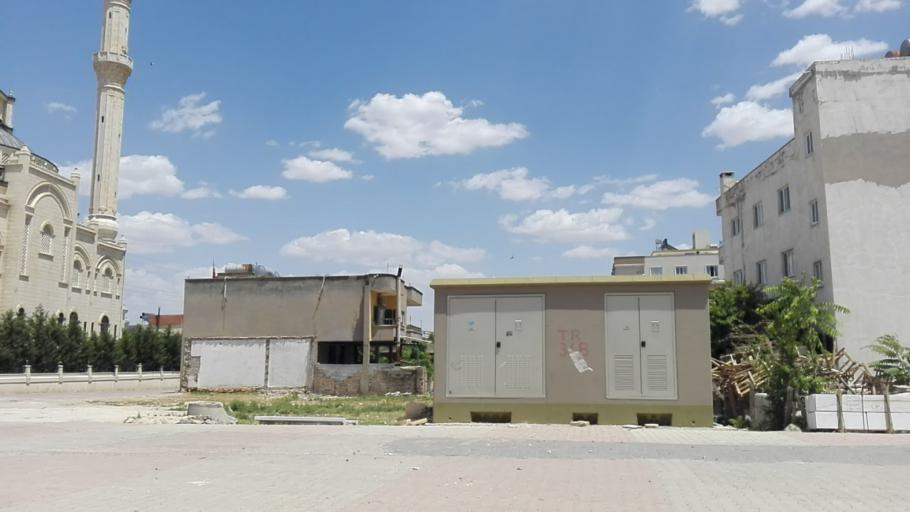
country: TR
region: Mardin
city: Midyat
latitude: 37.4184
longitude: 41.3608
